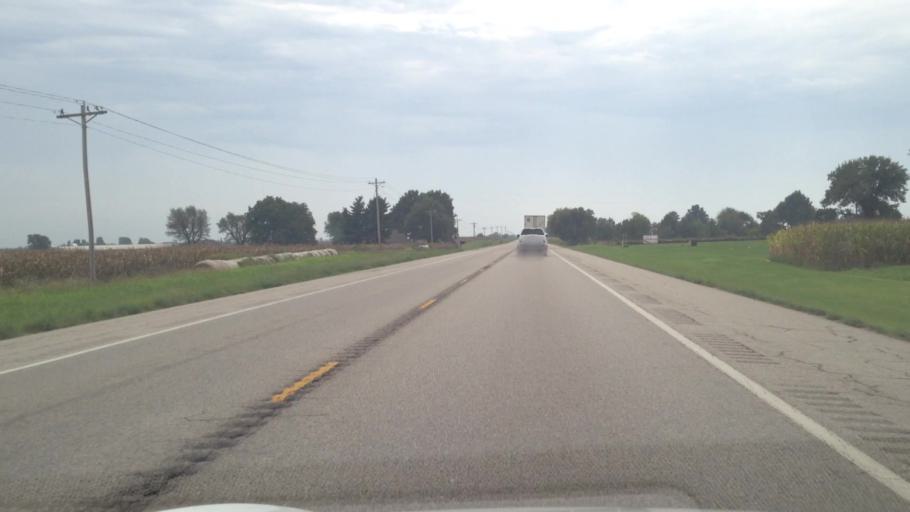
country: US
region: Kansas
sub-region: Crawford County
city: Pittsburg
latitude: 37.2797
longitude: -94.7054
